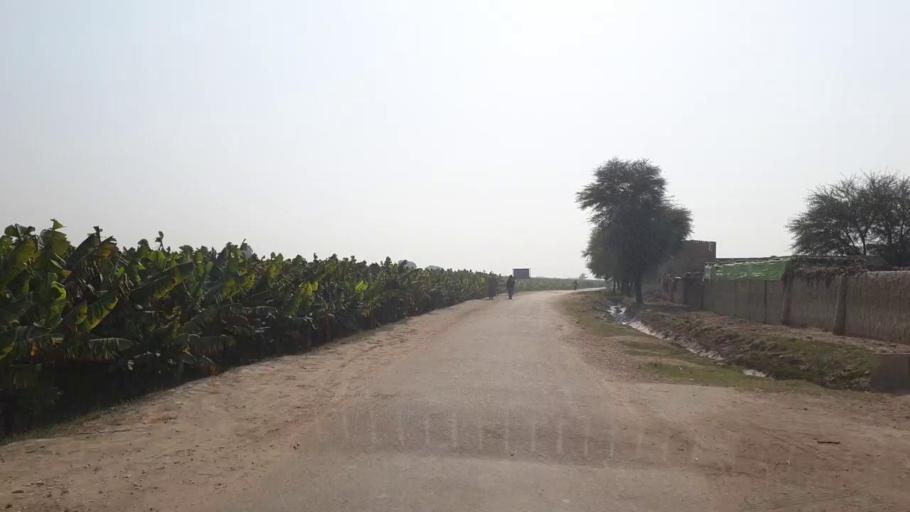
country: PK
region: Sindh
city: Bhit Shah
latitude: 25.7889
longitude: 68.4931
